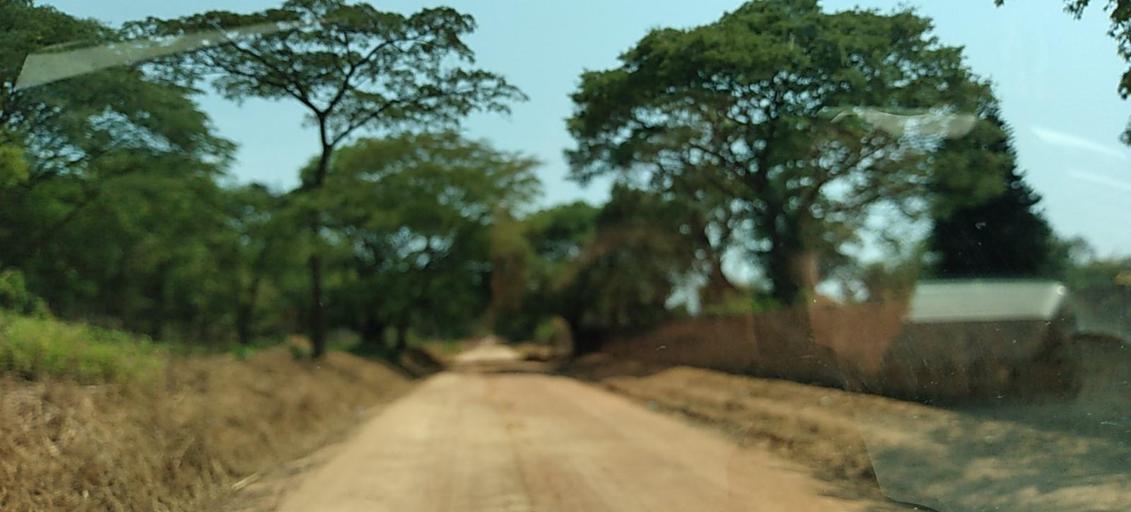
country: ZM
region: Copperbelt
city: Chingola
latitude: -12.6039
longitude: 27.9544
